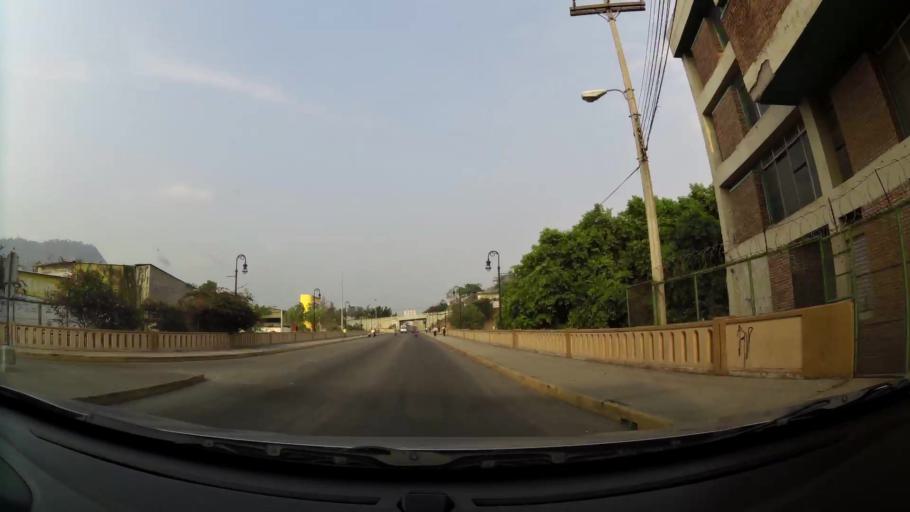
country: HN
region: Francisco Morazan
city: Tegucigalpa
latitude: 14.1005
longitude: -87.2061
